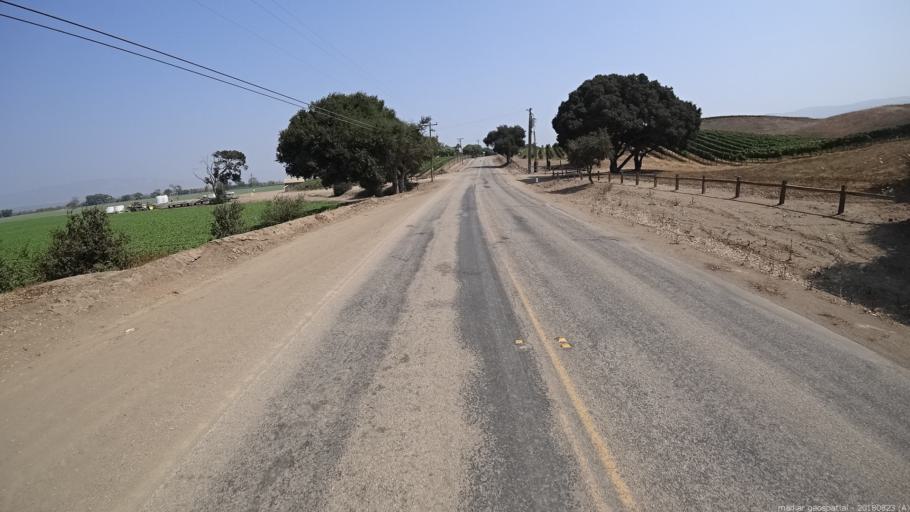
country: US
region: California
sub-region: Monterey County
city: Gonzales
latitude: 36.4687
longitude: -121.4607
